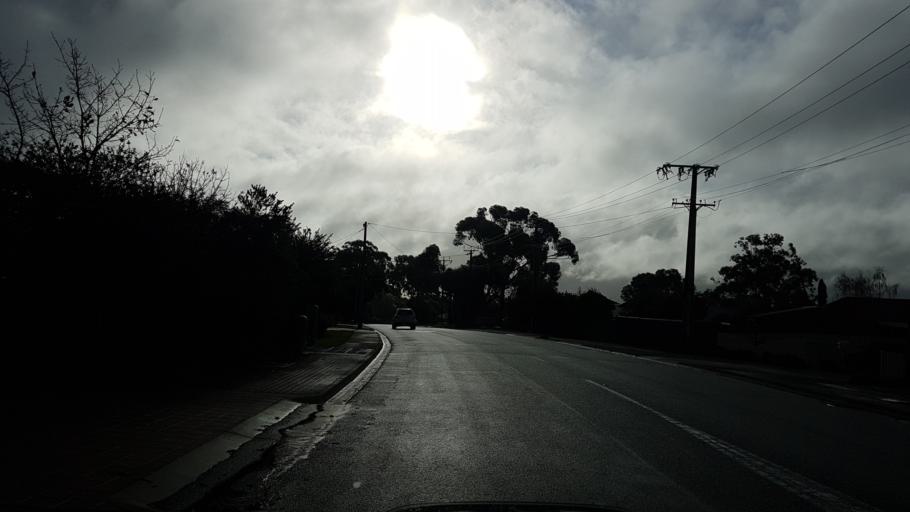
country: AU
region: South Australia
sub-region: Onkaparinga
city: Craigburn Farm
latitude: -35.0642
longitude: 138.6086
